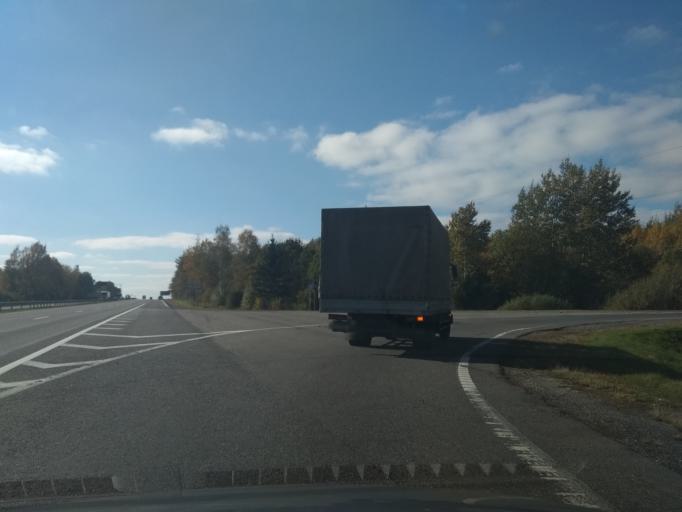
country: BY
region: Minsk
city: Haradzyeya
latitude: 53.3808
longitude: 26.5081
